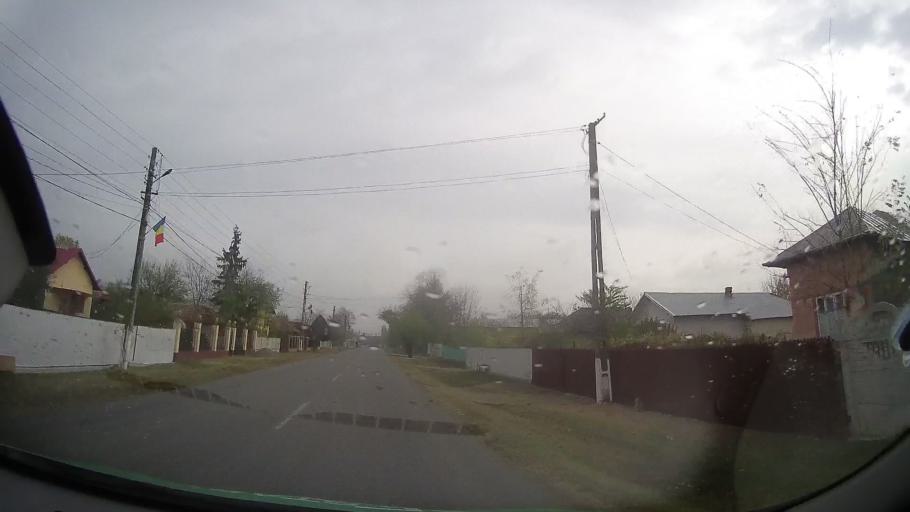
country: RO
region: Prahova
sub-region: Comuna Rafov
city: Palanca
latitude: 44.8453
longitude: 26.2319
